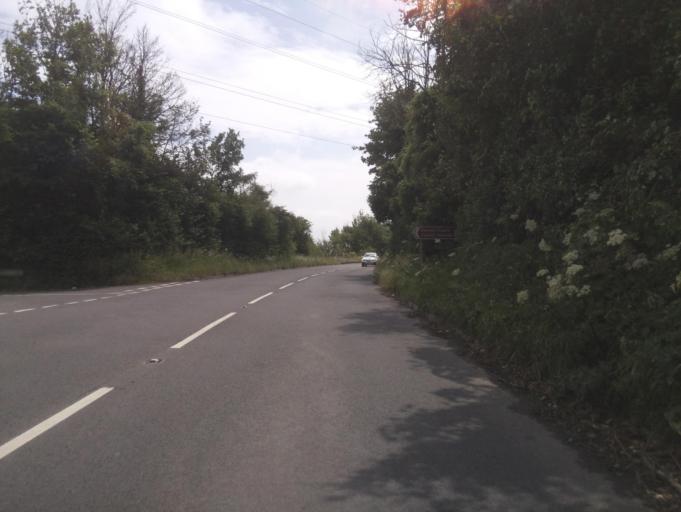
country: GB
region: Wales
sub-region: Vale of Glamorgan
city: Rhoose
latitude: 51.3977
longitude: -3.3884
